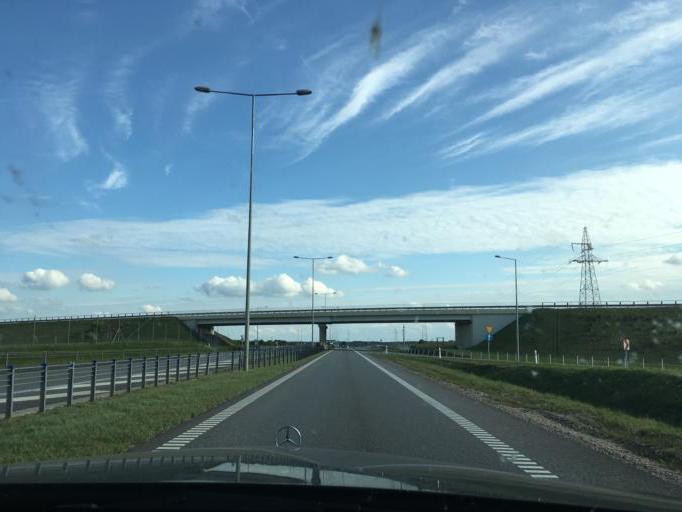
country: PL
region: Podlasie
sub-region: Powiat augustowski
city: Augustow
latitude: 53.8453
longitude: 22.9433
